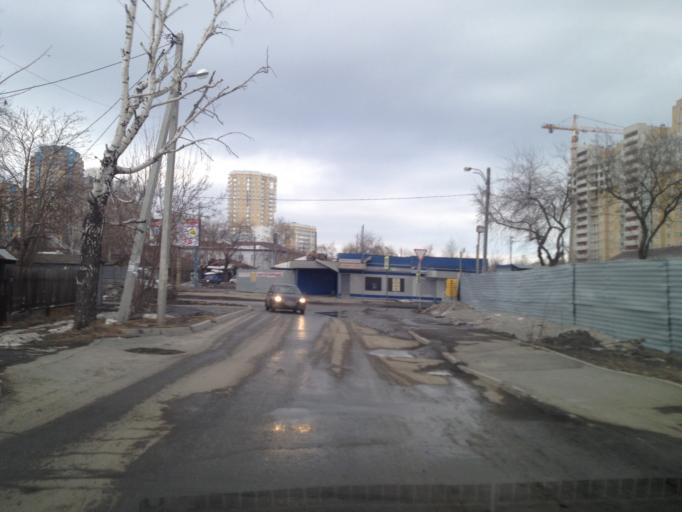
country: RU
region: Sverdlovsk
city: Yekaterinburg
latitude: 56.8015
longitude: 60.5932
